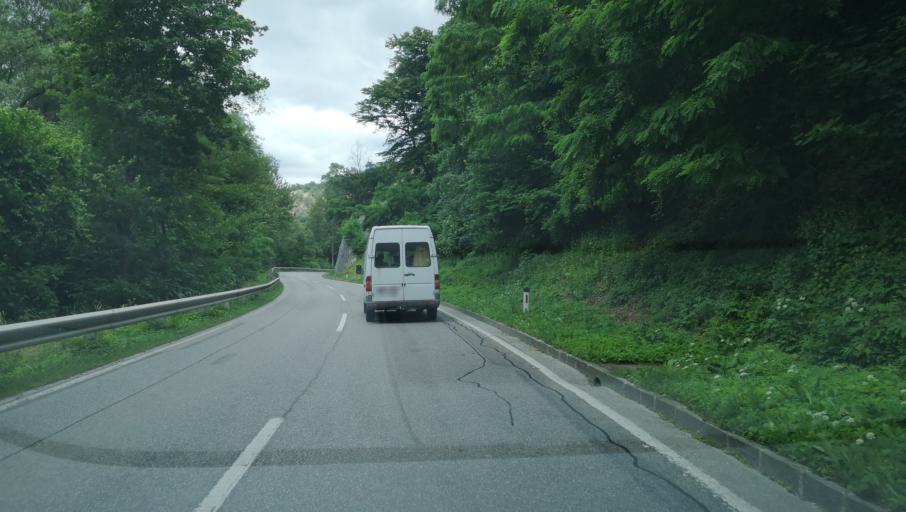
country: AT
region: Lower Austria
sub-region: Politischer Bezirk Krems
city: Aggsbach
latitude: 48.2790
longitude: 15.4010
